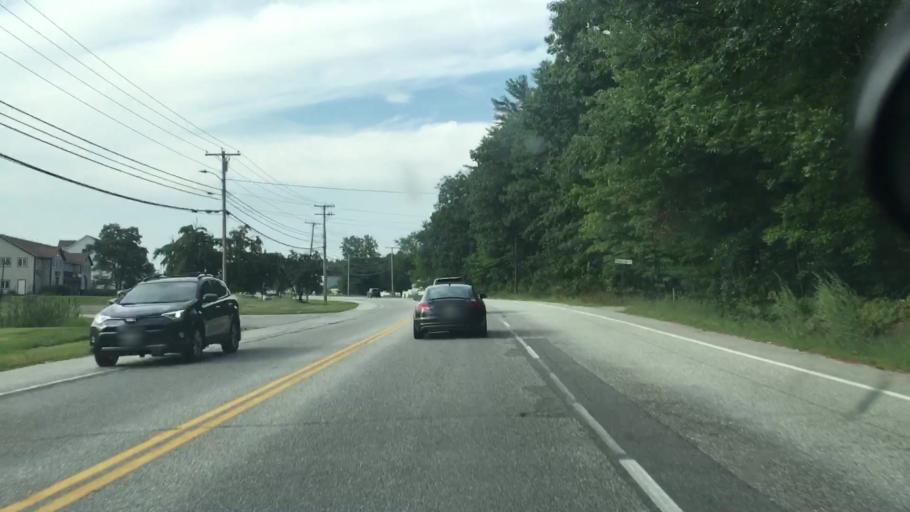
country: US
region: Maine
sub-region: Cumberland County
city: North Windham
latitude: 43.8540
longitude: -70.4511
